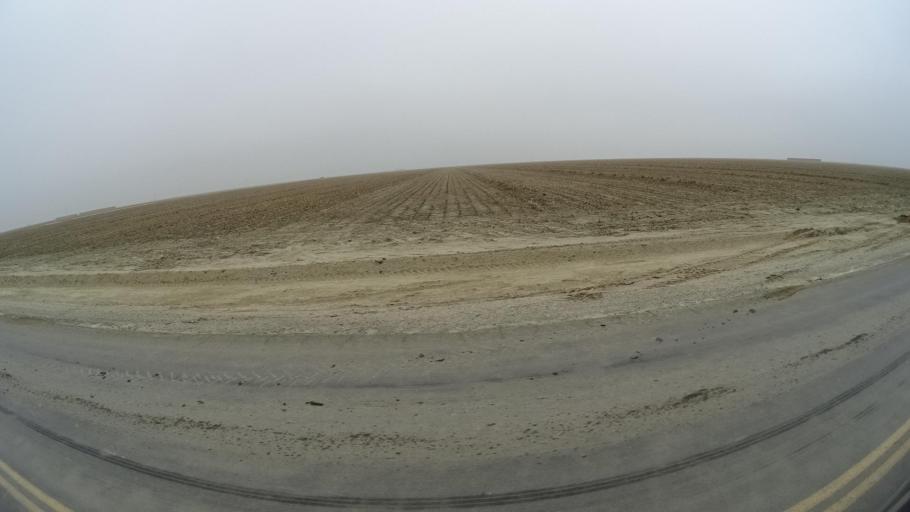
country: US
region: California
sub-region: Kern County
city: Rosedale
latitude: 35.2362
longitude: -119.2328
